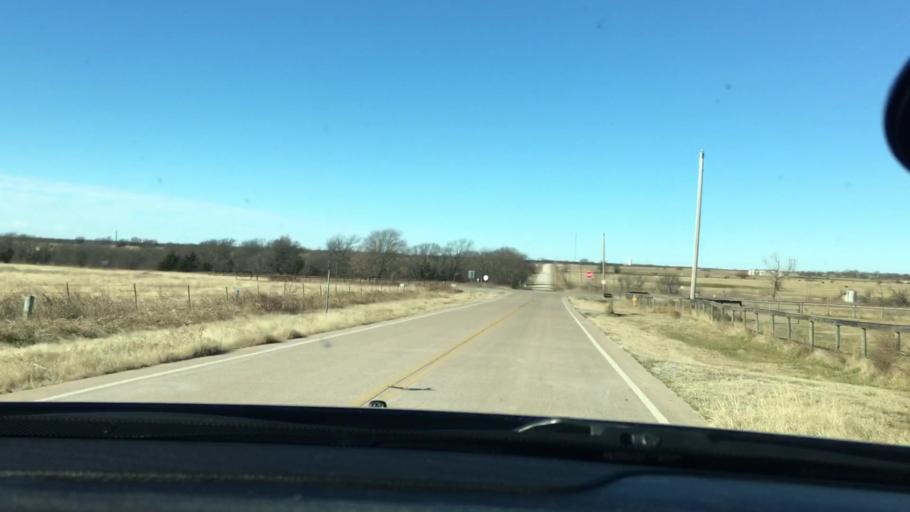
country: US
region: Oklahoma
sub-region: Marshall County
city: Madill
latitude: 34.1145
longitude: -96.7366
